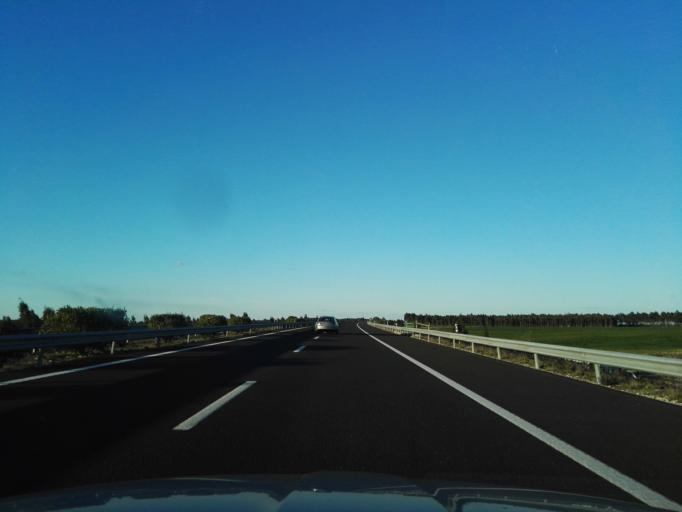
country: PT
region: Santarem
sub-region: Benavente
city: Poceirao
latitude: 38.7551
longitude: -8.6841
